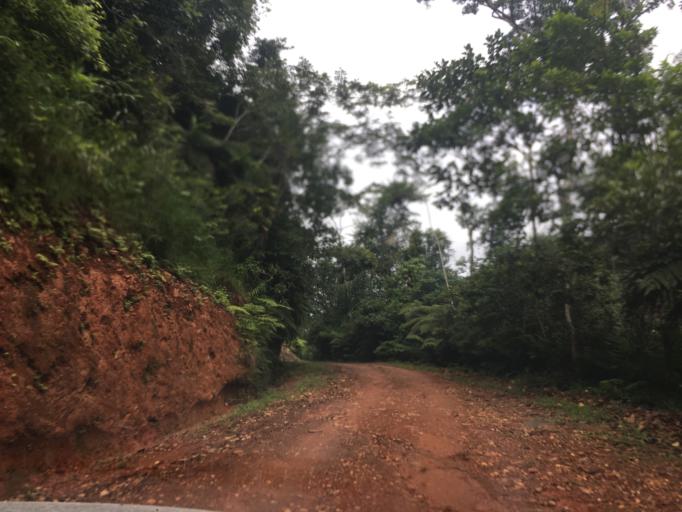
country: BZ
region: Stann Creek
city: Placencia
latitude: 16.7450
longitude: -88.4477
